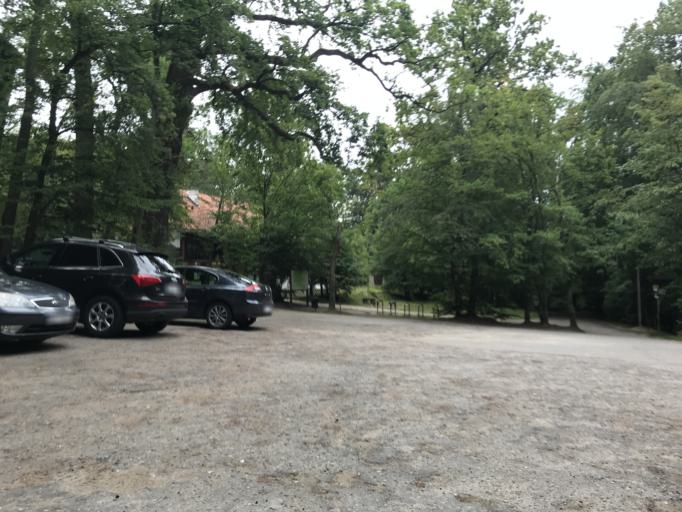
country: PL
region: Warmian-Masurian Voivodeship
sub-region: Powiat elblaski
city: Gronowo Gorne
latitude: 54.1737
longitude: 19.4444
